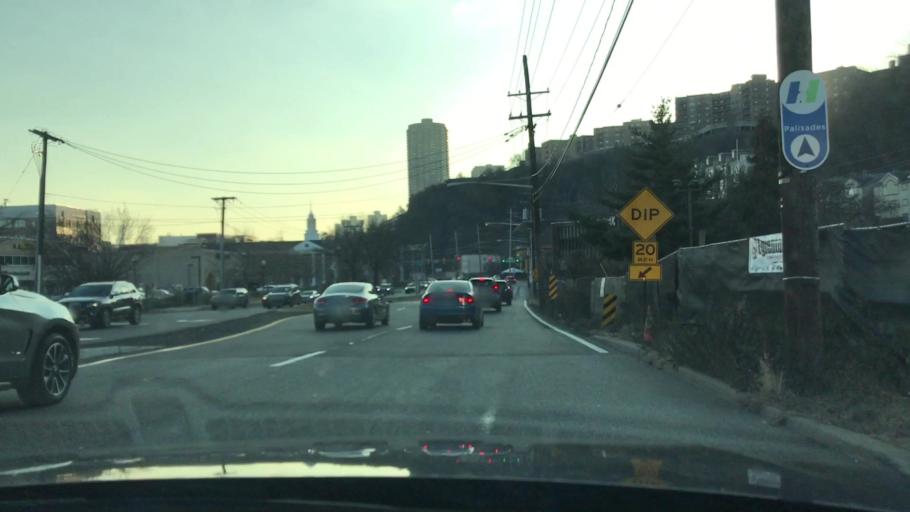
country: US
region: New Jersey
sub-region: Bergen County
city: Fairview
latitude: 40.8059
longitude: -73.9920
